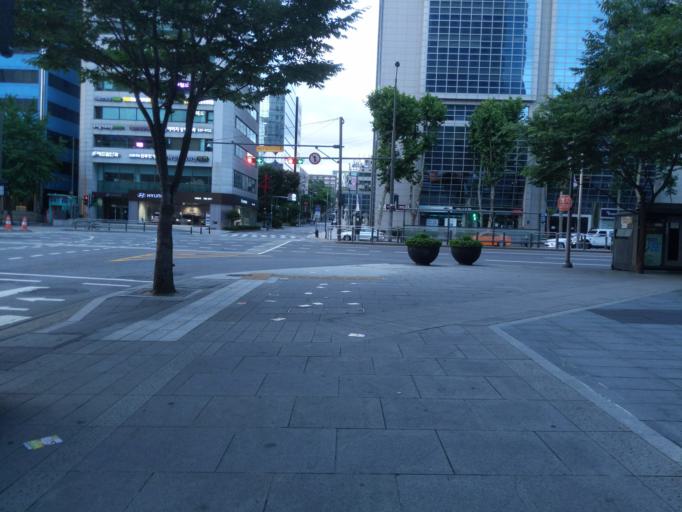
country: KR
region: Seoul
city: Seoul
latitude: 37.5080
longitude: 127.0590
